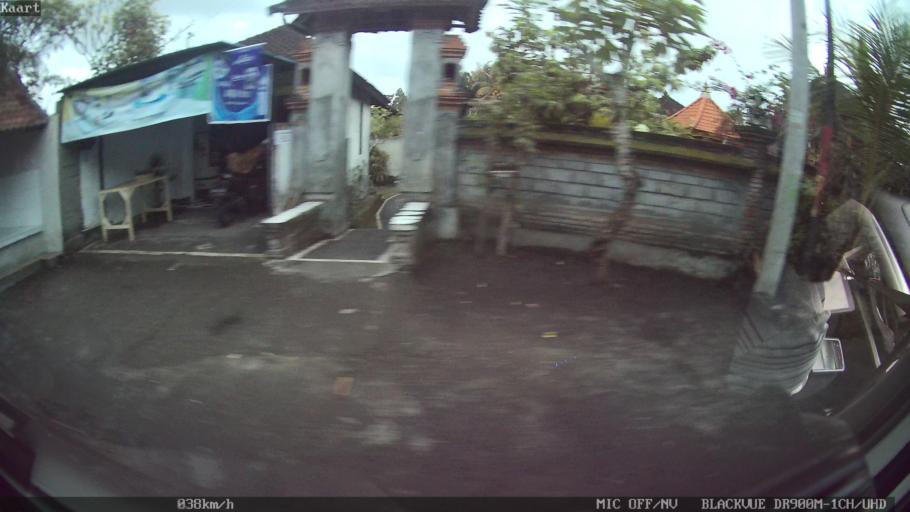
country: ID
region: Bali
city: Banjar Tebongkang
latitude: -8.5284
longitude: 115.2371
